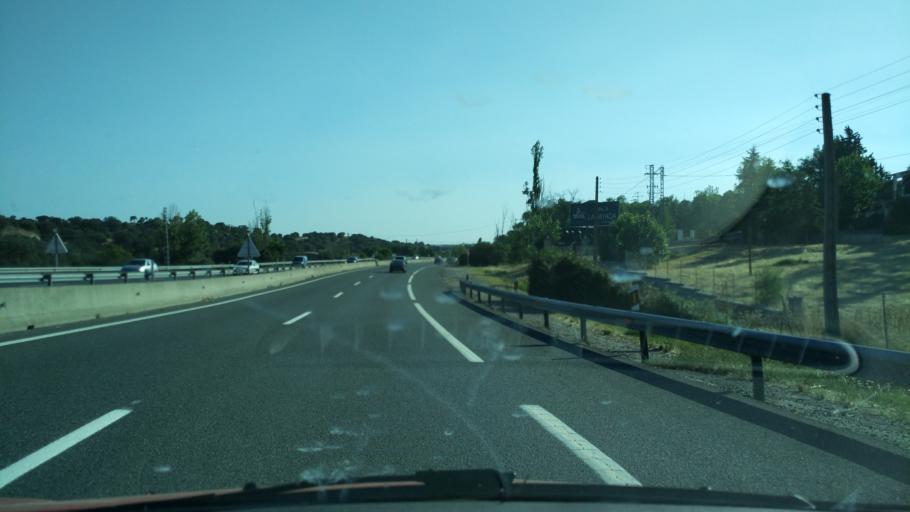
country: ES
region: Madrid
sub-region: Provincia de Madrid
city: San Agustin de Guadalix
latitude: 40.6952
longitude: -3.5895
